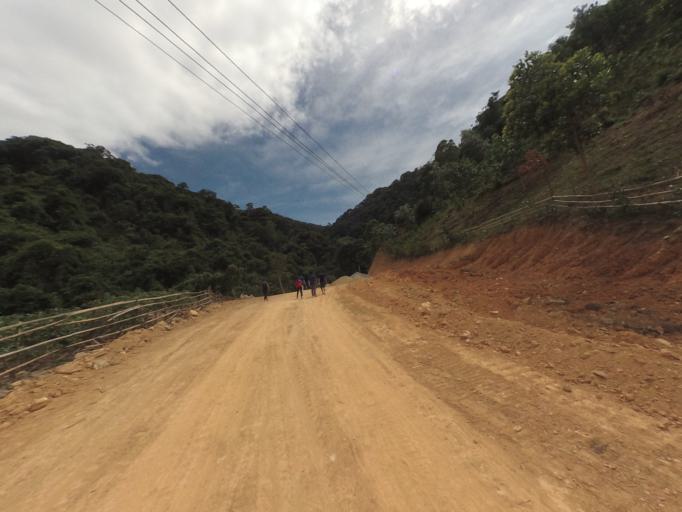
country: VN
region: Thua Thien-Hue
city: A Luoi
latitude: 16.3068
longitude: 107.2160
